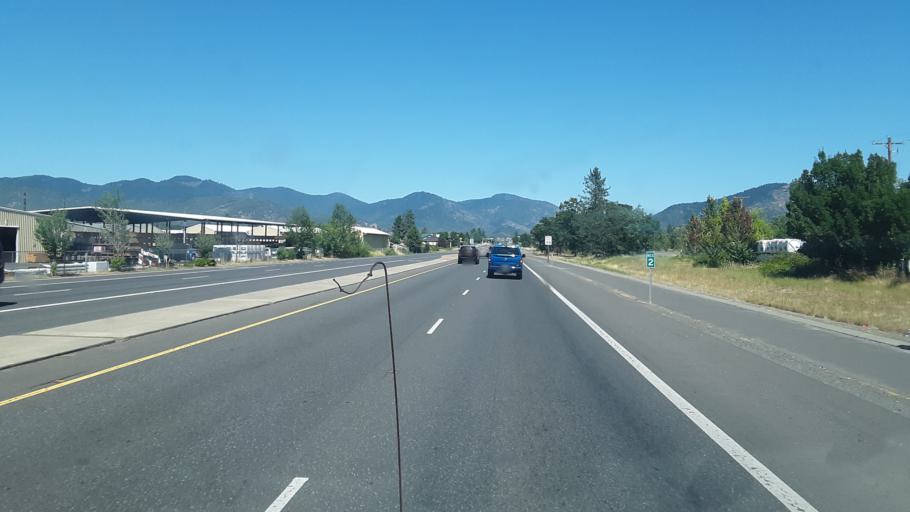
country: US
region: Oregon
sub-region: Josephine County
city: Redwood
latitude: 42.4186
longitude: -123.3663
